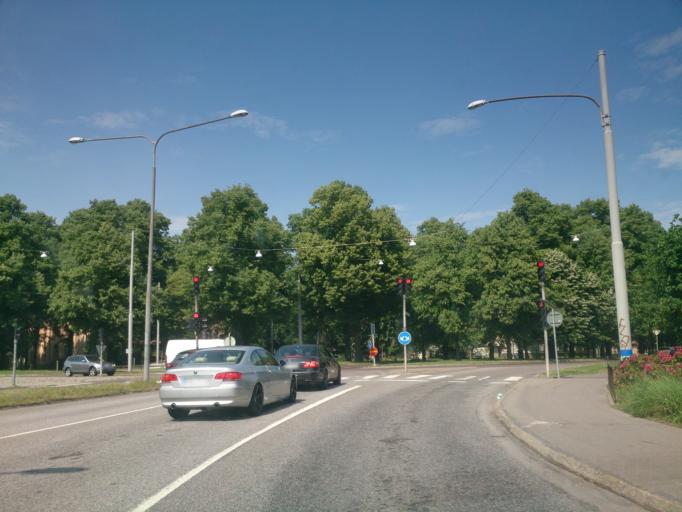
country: SE
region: OEstergoetland
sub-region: Norrkopings Kommun
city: Norrkoping
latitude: 58.5855
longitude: 16.2015
